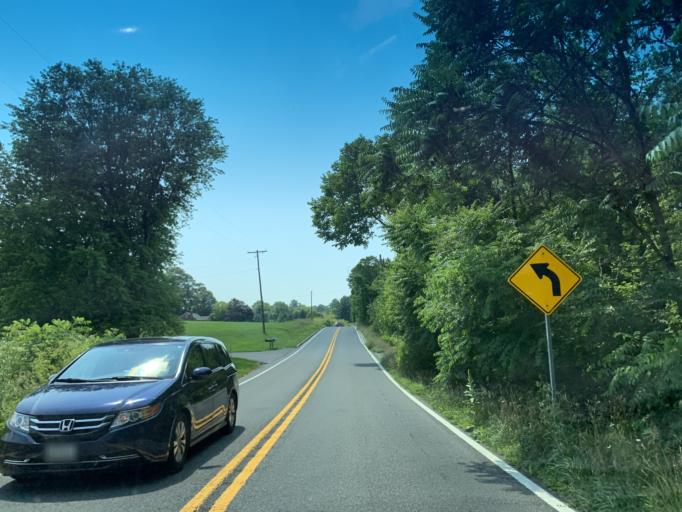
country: US
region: Maryland
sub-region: Frederick County
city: Green Valley
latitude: 39.2774
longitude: -77.3287
